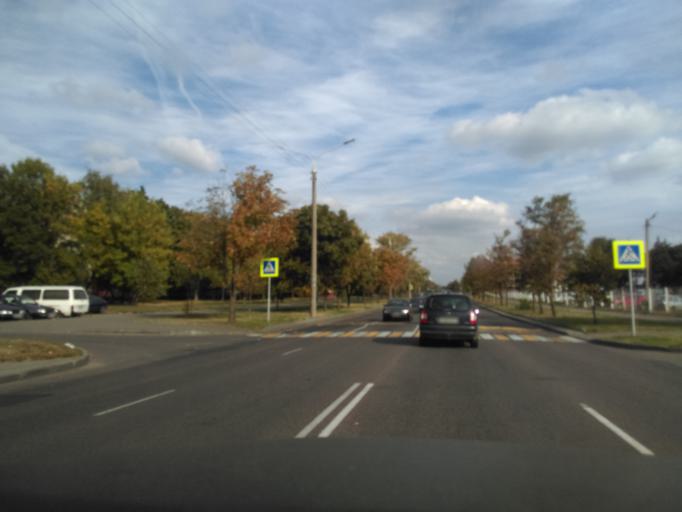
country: BY
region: Minsk
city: Machulishchy
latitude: 53.8342
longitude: 27.6129
